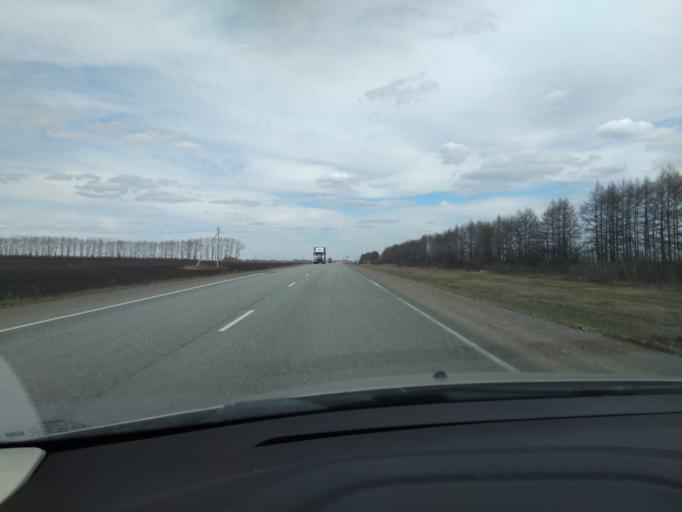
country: RU
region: Sverdlovsk
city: Yelanskiy
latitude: 56.7732
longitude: 62.4523
